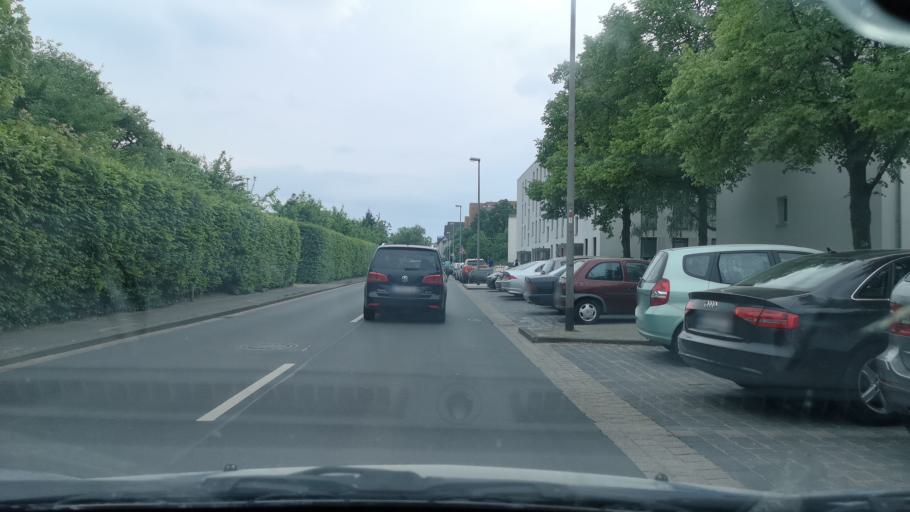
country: DE
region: Lower Saxony
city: Hannover
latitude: 52.4069
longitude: 9.6951
